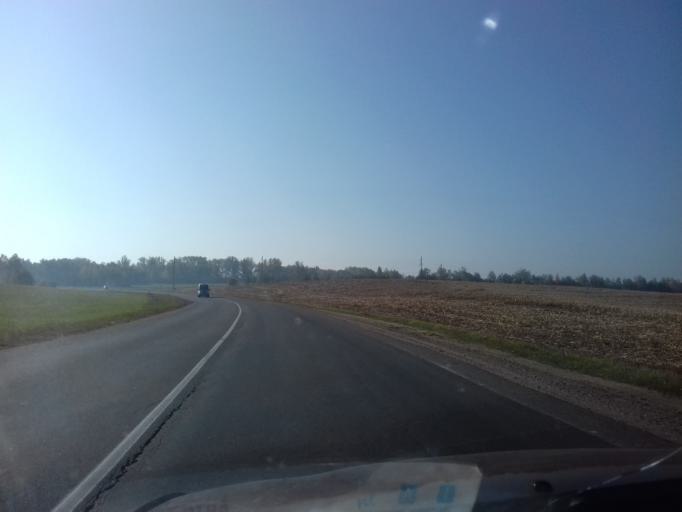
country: BY
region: Minsk
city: Hatava
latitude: 53.7720
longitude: 27.6374
